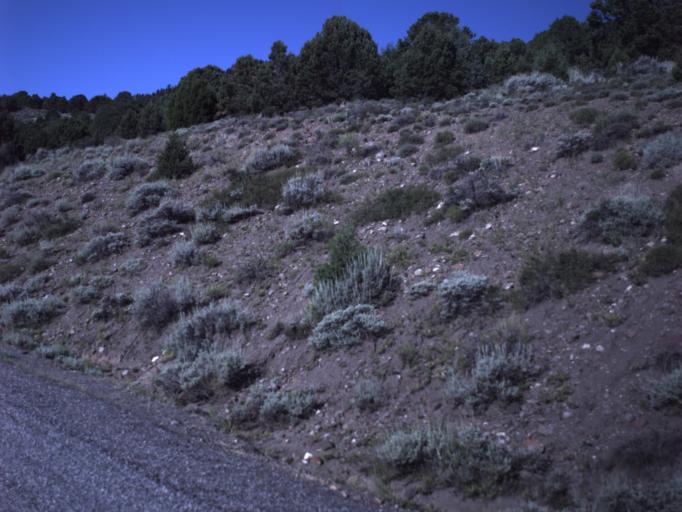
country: US
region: Utah
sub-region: Wayne County
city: Loa
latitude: 38.6104
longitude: -111.4608
